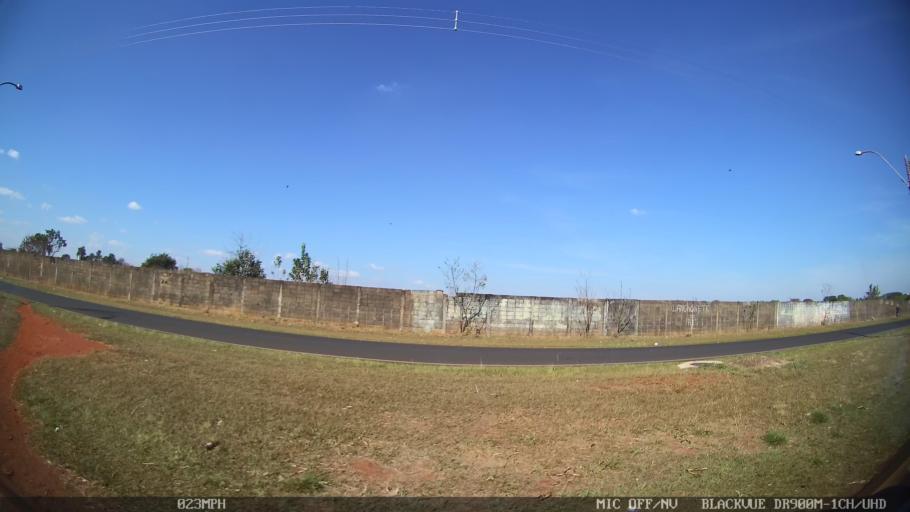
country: BR
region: Sao Paulo
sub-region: Ribeirao Preto
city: Ribeirao Preto
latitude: -21.1468
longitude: -47.7705
